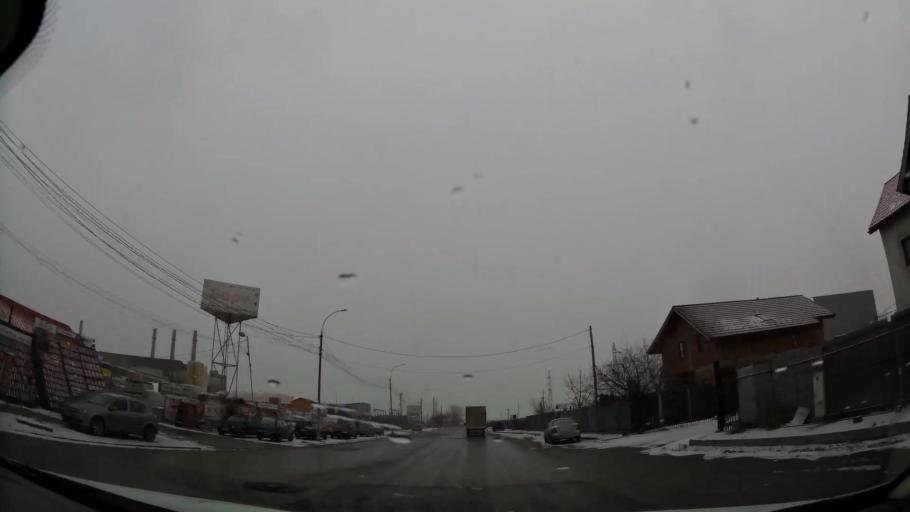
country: RO
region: Dambovita
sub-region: Municipiul Targoviste
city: Targoviste
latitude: 44.9274
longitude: 25.4323
